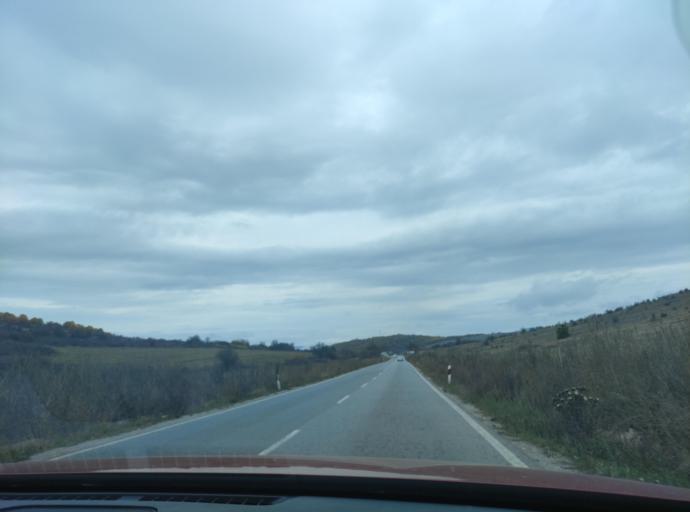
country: BG
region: Sofiya
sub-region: Obshtina Godech
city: Godech
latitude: 42.9573
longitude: 23.1562
